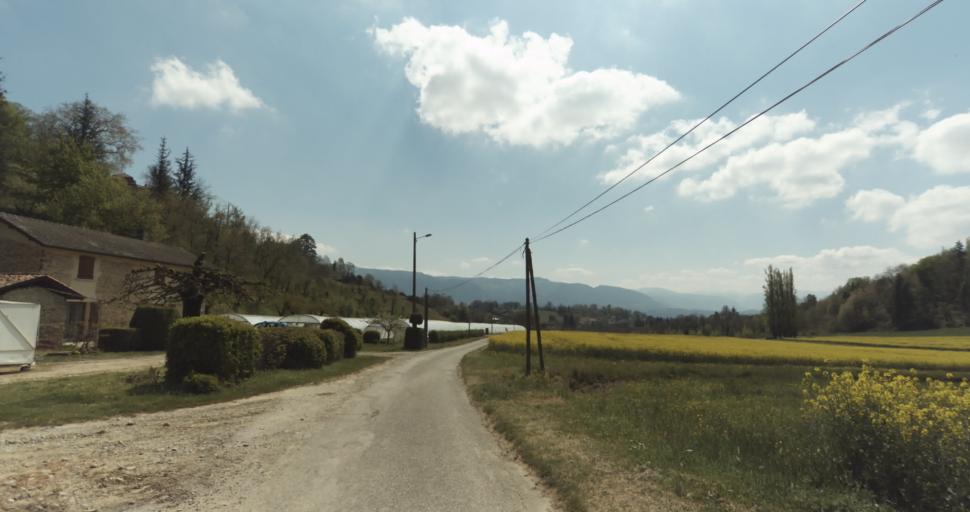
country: FR
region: Rhone-Alpes
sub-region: Departement de l'Isere
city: Saint-Verand
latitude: 45.1671
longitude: 5.3177
